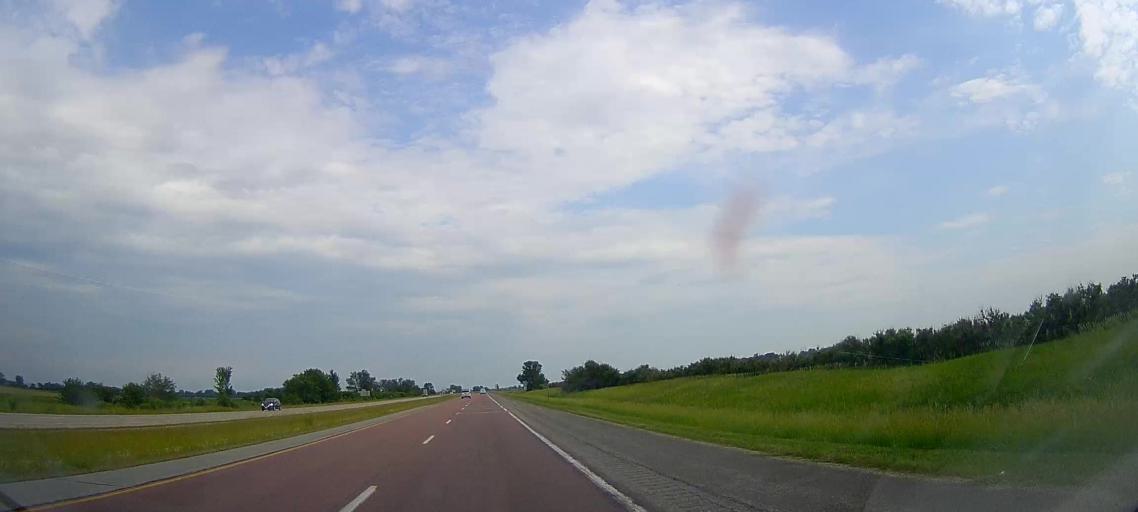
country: US
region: Iowa
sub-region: Monona County
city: Onawa
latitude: 42.0209
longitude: -96.1279
